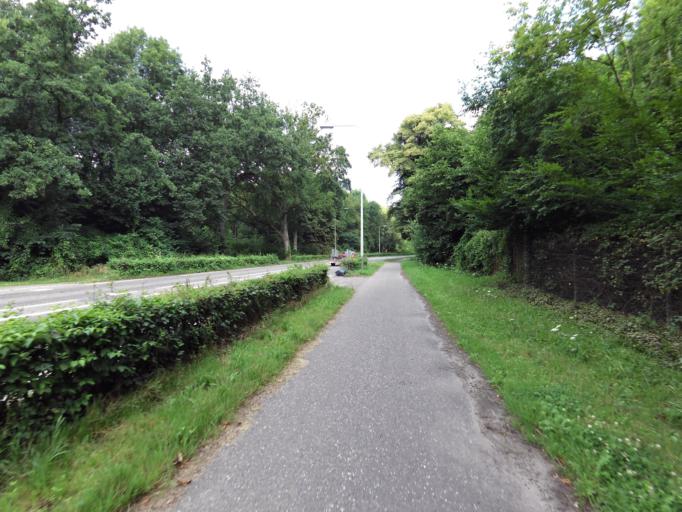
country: NL
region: Limburg
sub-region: Gemeente Voerendaal
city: Voerendaal
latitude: 50.8893
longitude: 5.9296
